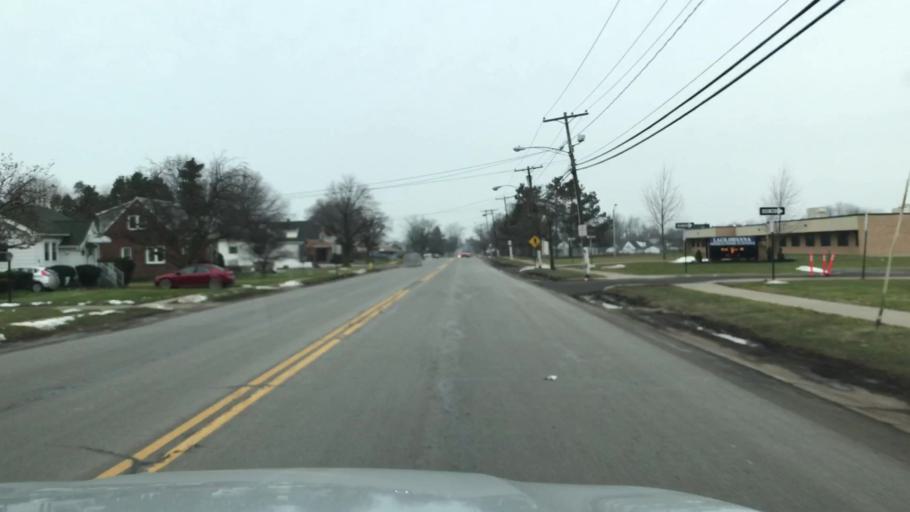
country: US
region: New York
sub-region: Erie County
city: Lackawanna
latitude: 42.8166
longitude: -78.8030
